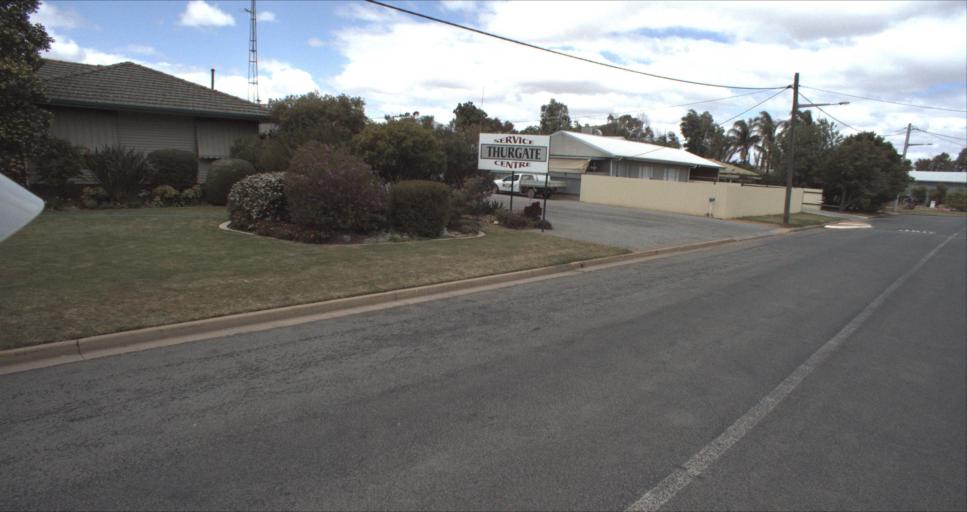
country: AU
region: New South Wales
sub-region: Leeton
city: Leeton
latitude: -34.5543
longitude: 146.3929
